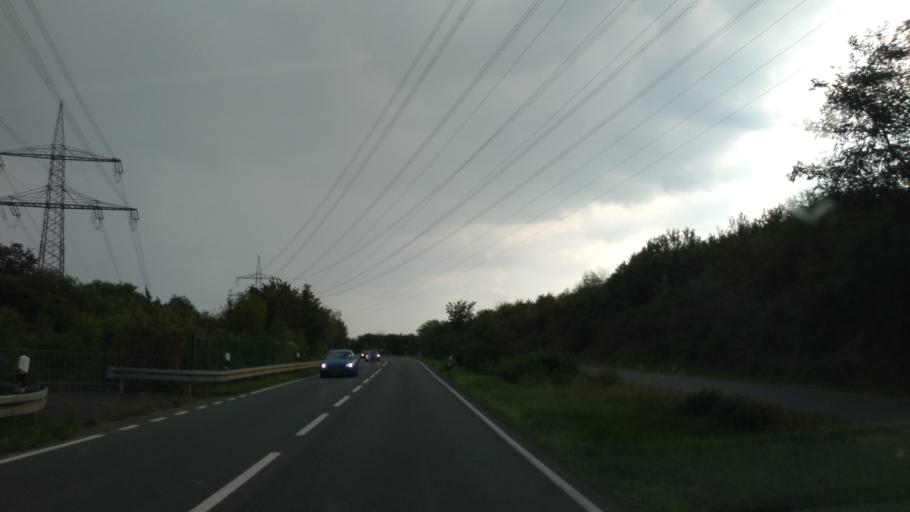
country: DE
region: North Rhine-Westphalia
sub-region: Regierungsbezirk Koln
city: Alfter
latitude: 50.7366
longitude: 7.0332
